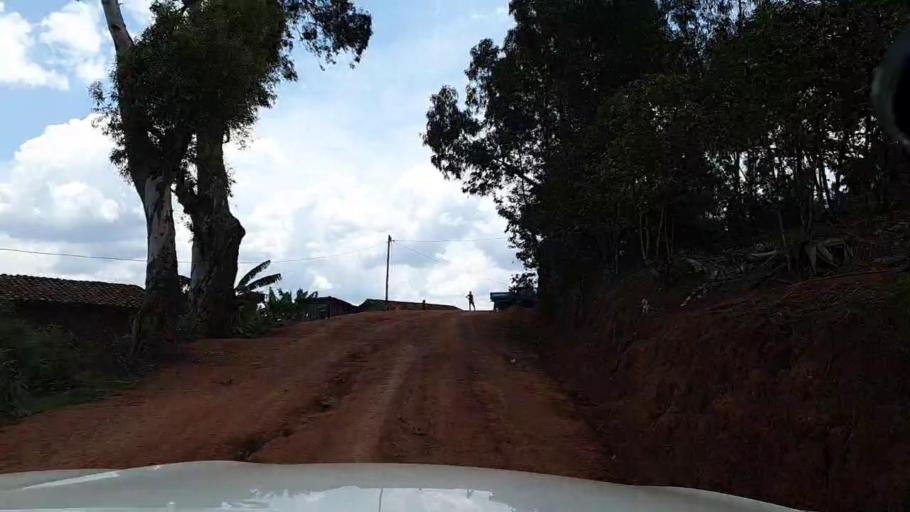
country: RW
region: Southern Province
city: Butare
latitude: -2.7547
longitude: 29.7533
